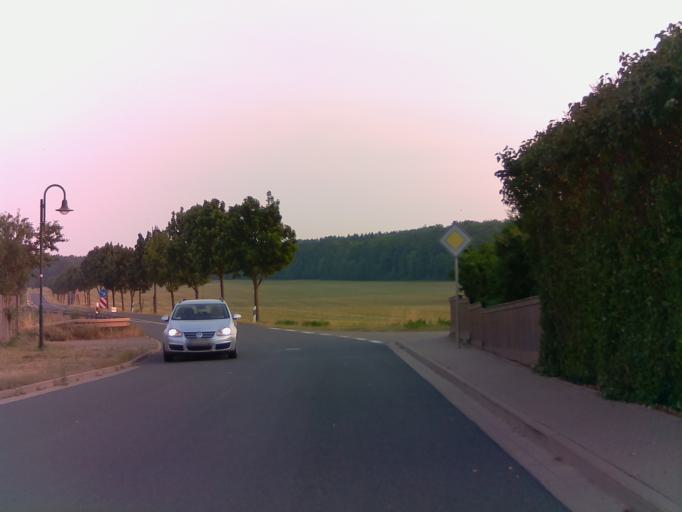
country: DE
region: Thuringia
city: Troistedt
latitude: 50.9379
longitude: 11.2463
